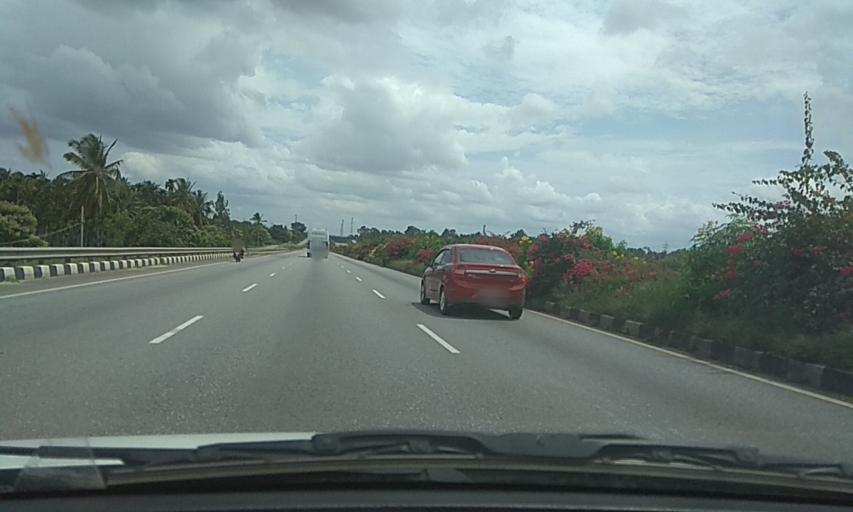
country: IN
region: Karnataka
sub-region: Tumkur
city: Tumkur
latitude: 13.5243
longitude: 77.0009
